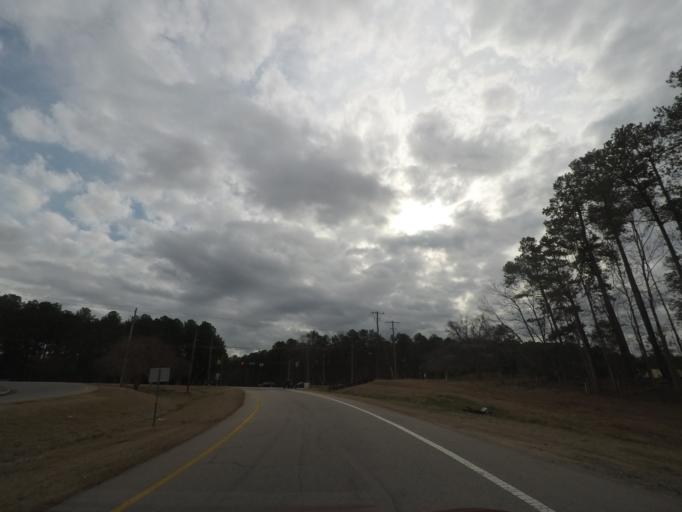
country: US
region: North Carolina
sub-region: Wake County
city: Morrisville
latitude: 35.8495
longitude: -78.8002
